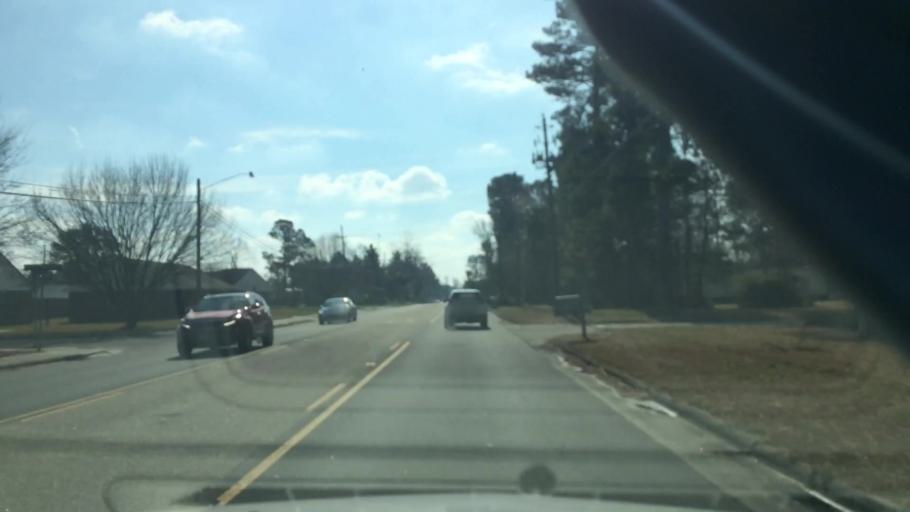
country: US
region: North Carolina
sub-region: Duplin County
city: Beulaville
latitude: 34.9199
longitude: -77.7747
